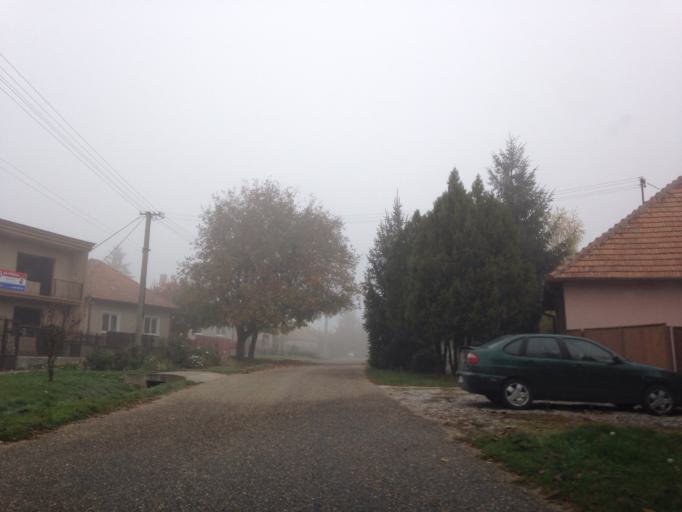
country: SK
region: Nitriansky
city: Svodin
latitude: 47.9072
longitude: 18.4148
